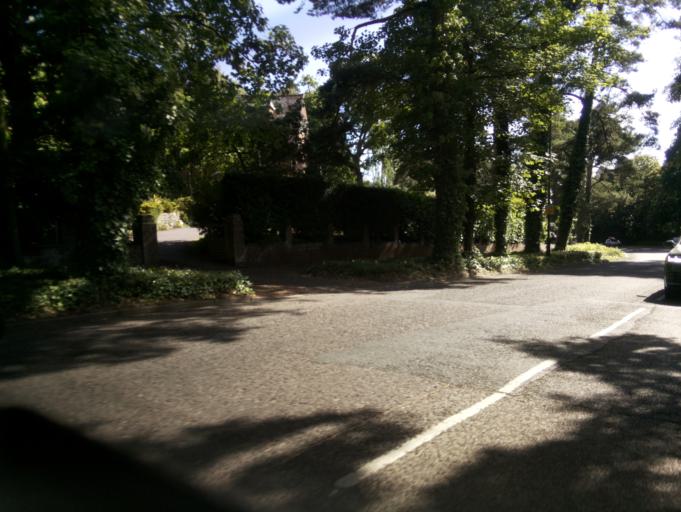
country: GB
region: England
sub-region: Bournemouth
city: Bournemouth
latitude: 50.7290
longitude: -1.8964
